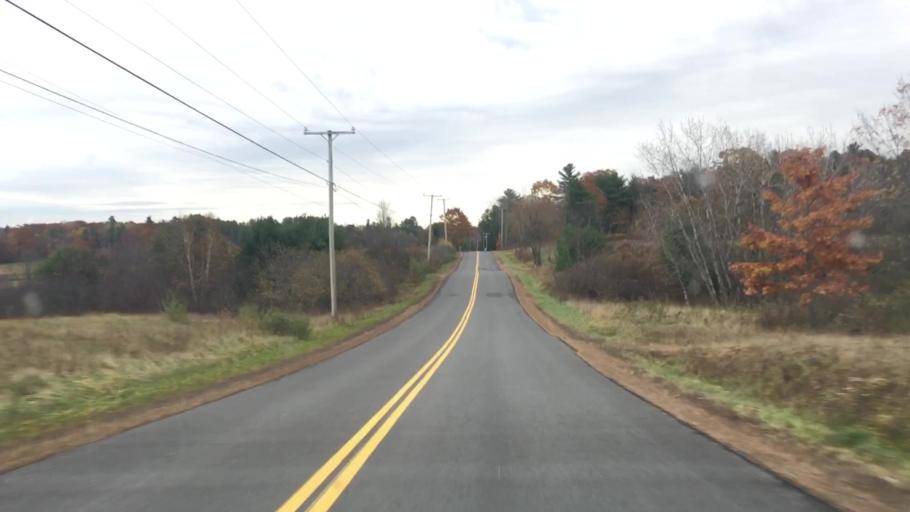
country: US
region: Maine
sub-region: Kennebec County
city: Pittston
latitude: 44.1694
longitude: -69.7179
